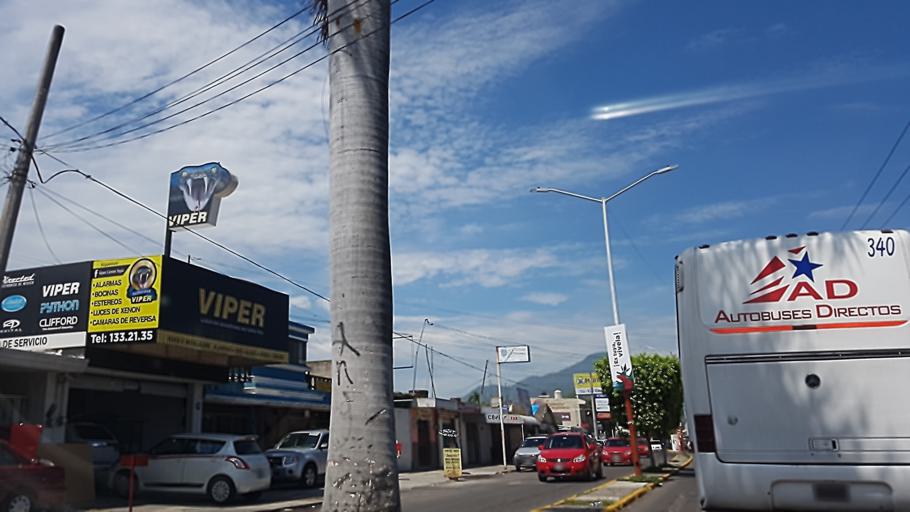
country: MX
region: Nayarit
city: Tepic
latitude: 21.4848
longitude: -104.8774
